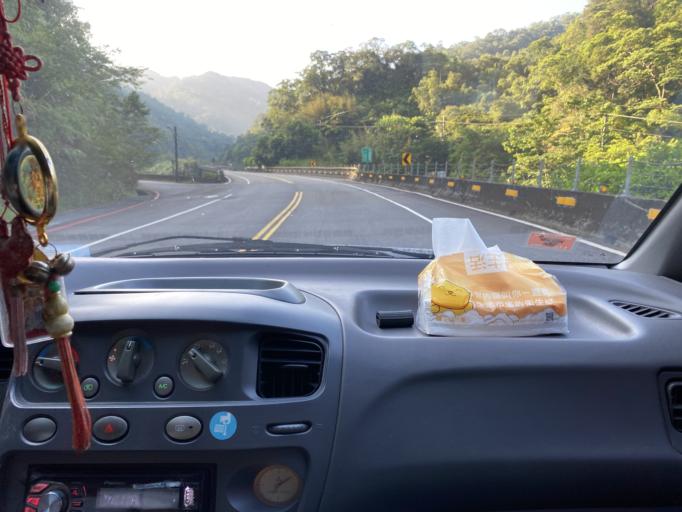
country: TW
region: Taiwan
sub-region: Keelung
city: Keelung
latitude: 25.0317
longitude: 121.7787
